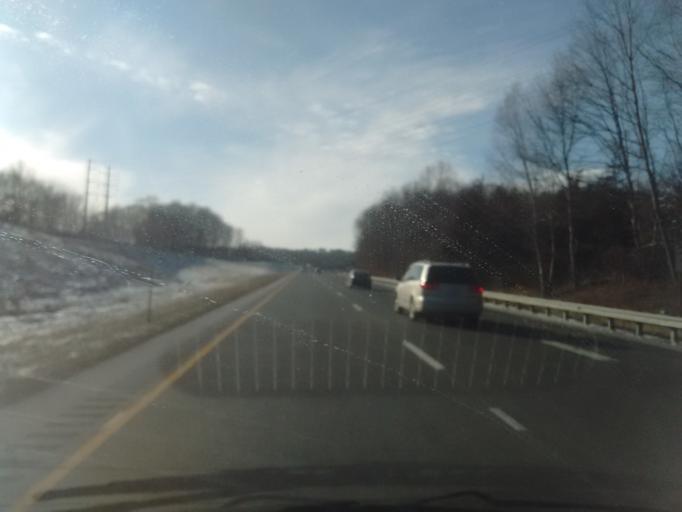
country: US
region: Connecticut
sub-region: New Haven County
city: Middlebury
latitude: 41.5203
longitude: -73.0982
